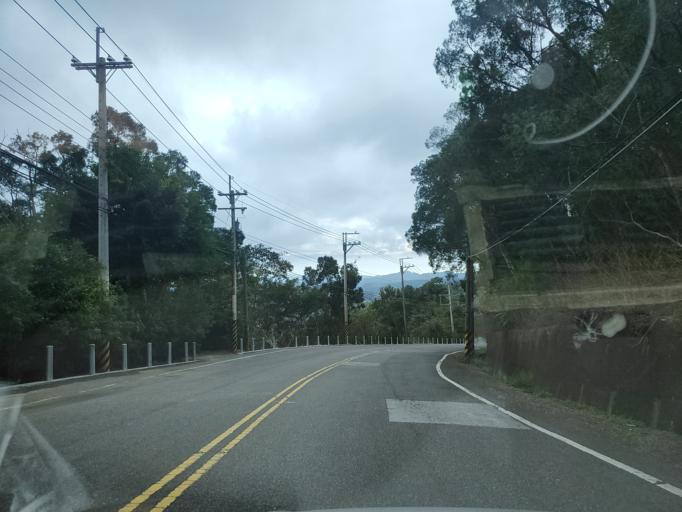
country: TW
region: Taiwan
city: Fengyuan
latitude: 24.3738
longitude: 120.7752
